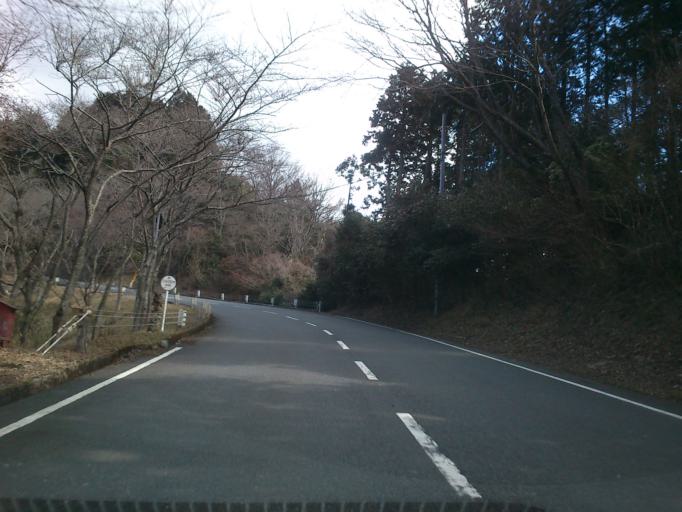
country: JP
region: Shiga Prefecture
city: Otsu-shi
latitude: 35.0372
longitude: 135.8376
